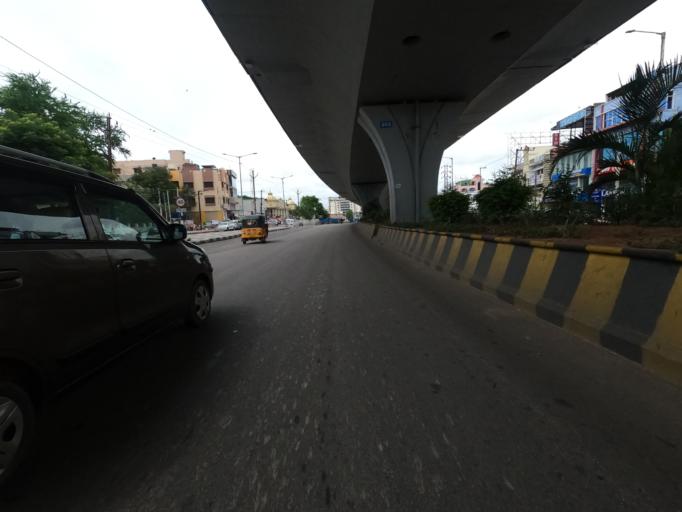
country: IN
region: Telangana
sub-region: Hyderabad
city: Hyderabad
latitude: 17.3925
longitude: 78.4311
